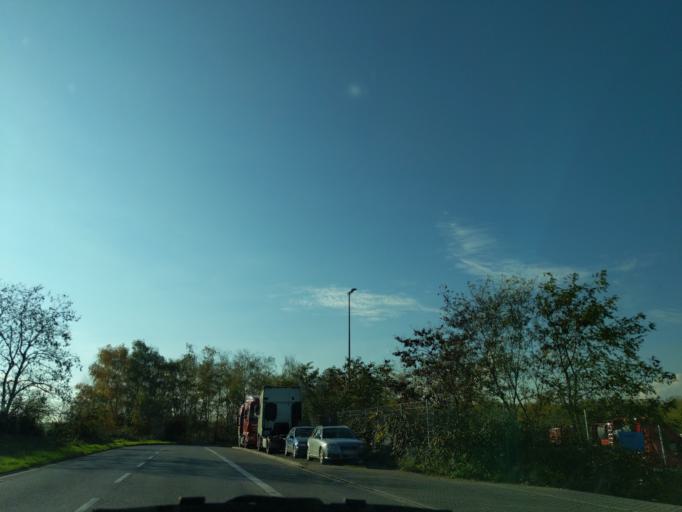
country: DE
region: North Rhine-Westphalia
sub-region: Regierungsbezirk Koln
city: Leverkusen
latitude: 51.0184
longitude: 6.9373
